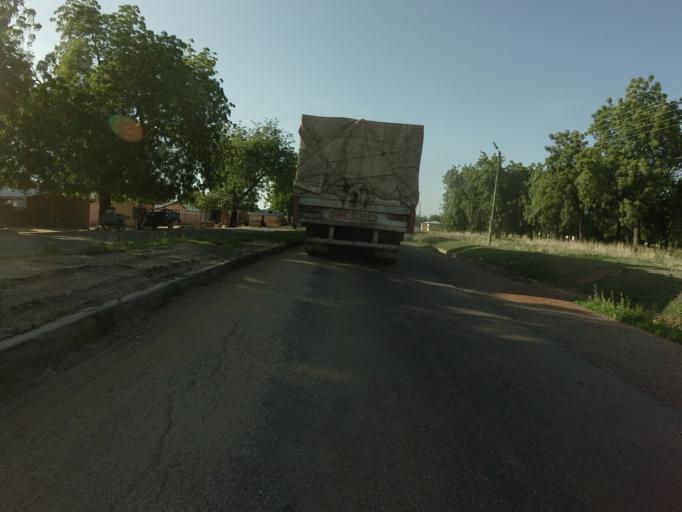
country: GH
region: Upper East
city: Navrongo
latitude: 10.8993
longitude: -1.0925
